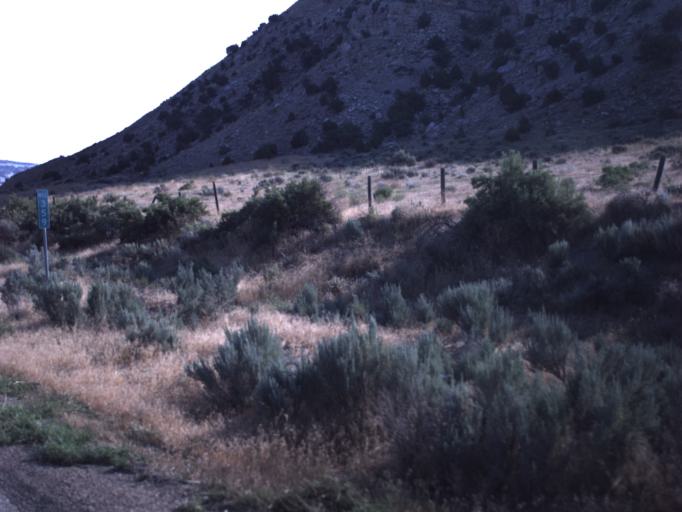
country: US
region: Utah
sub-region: Uintah County
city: Vernal
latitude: 40.5455
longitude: -109.5261
